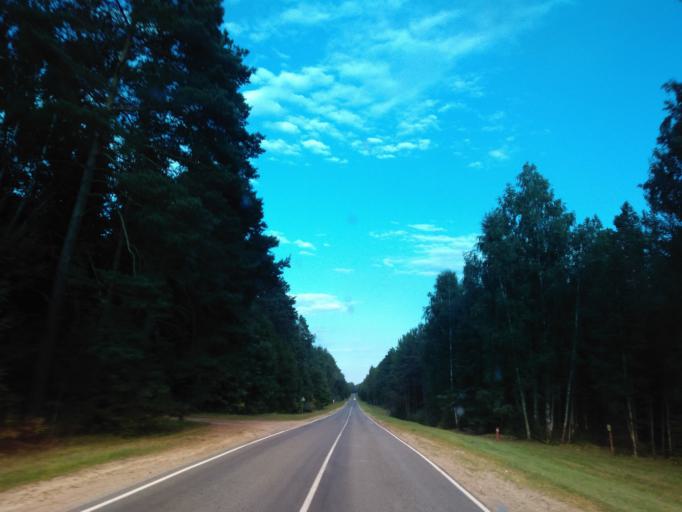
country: BY
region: Minsk
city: Uzda
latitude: 53.4253
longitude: 27.3726
